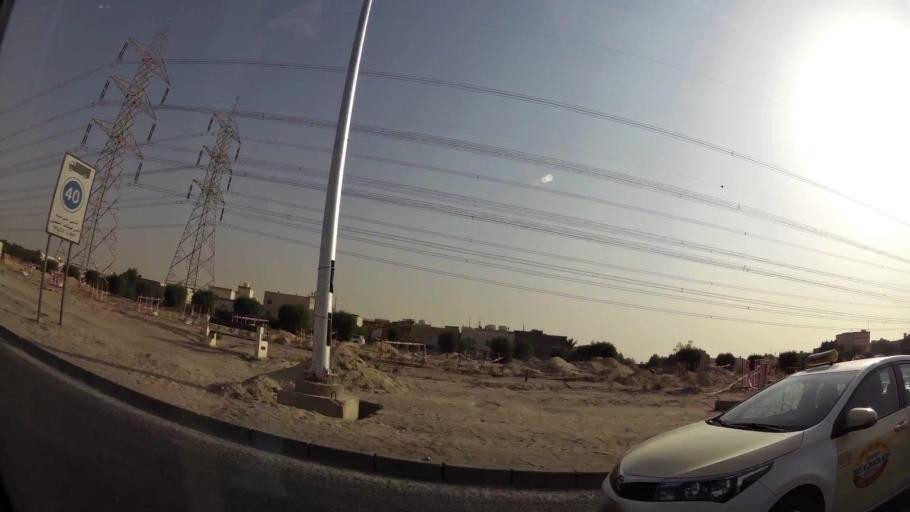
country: KW
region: Al Asimah
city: Ar Rabiyah
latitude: 29.2960
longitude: 47.8722
